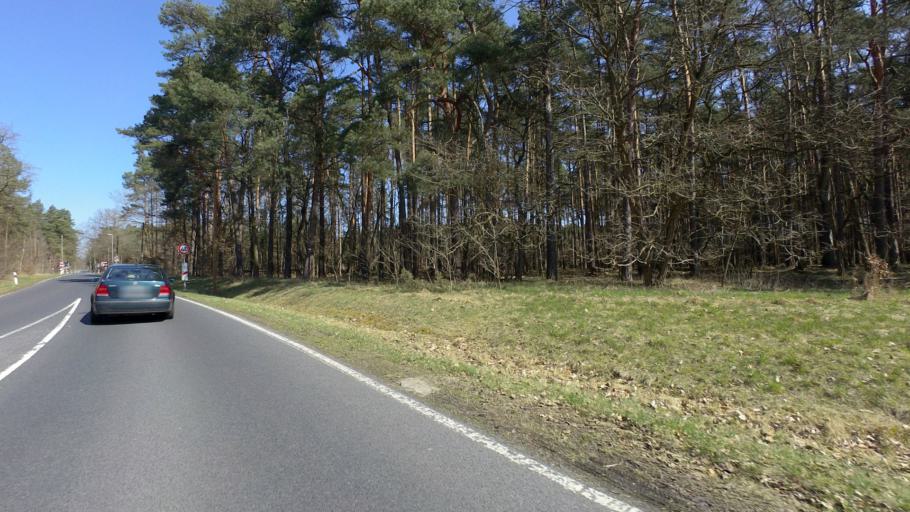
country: DE
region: Brandenburg
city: Ruthnick
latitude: 52.9100
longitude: 12.9564
